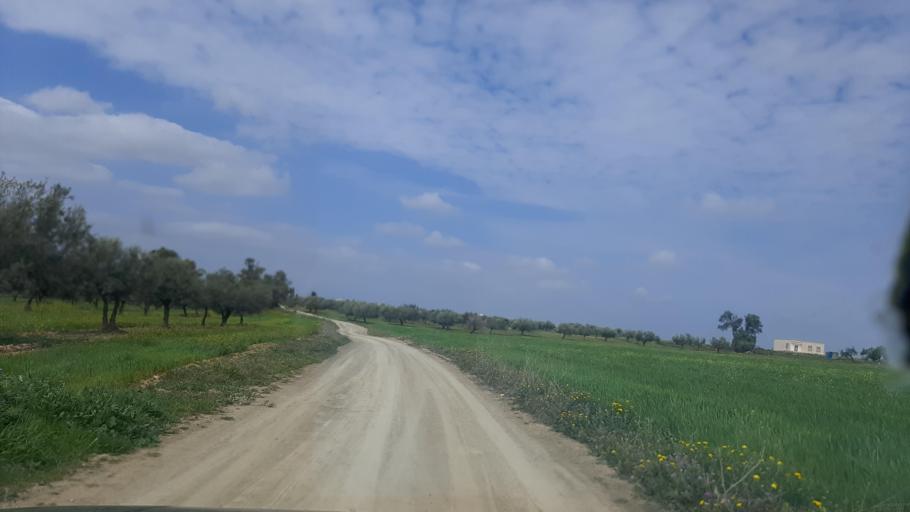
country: TN
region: Tunis
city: Oued Lill
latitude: 36.6881
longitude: 9.9963
